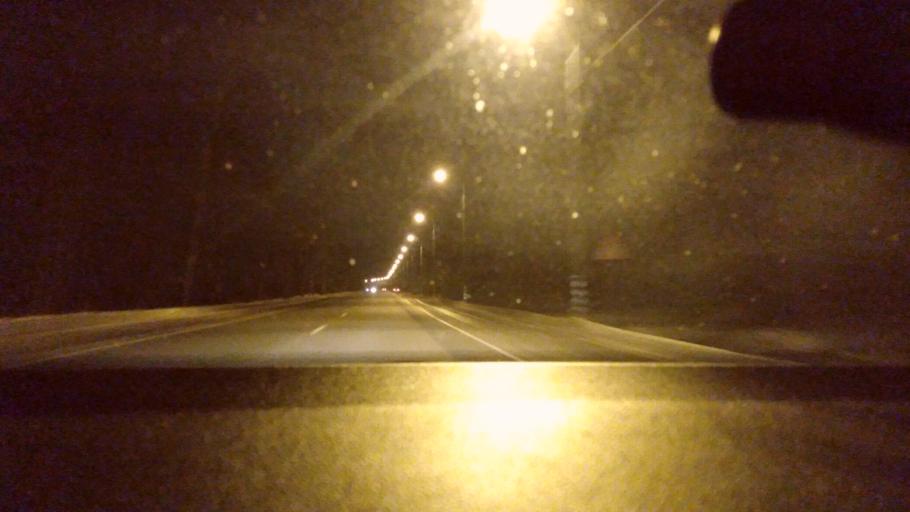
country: RU
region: Moskovskaya
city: Il'inskiy Pogost
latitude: 55.4825
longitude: 38.9302
